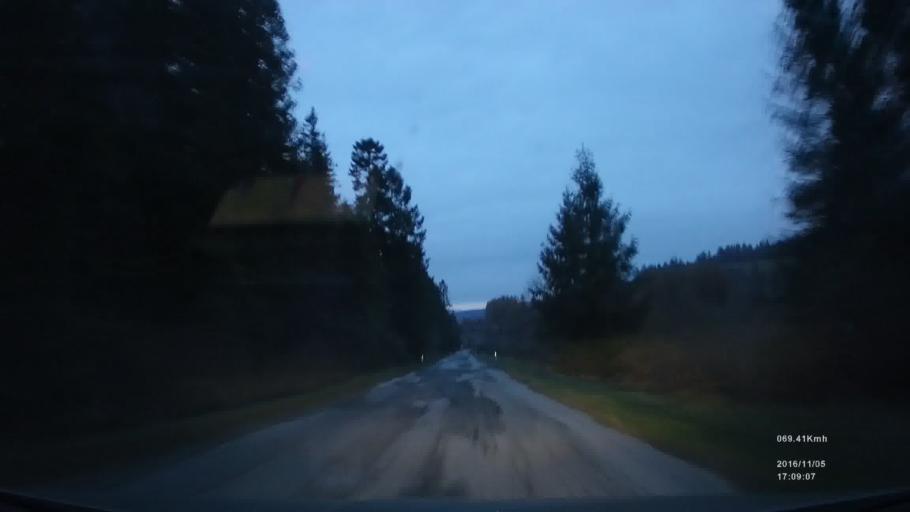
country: SK
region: Presovsky
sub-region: Okres Presov
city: Levoca
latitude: 49.0512
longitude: 20.5175
